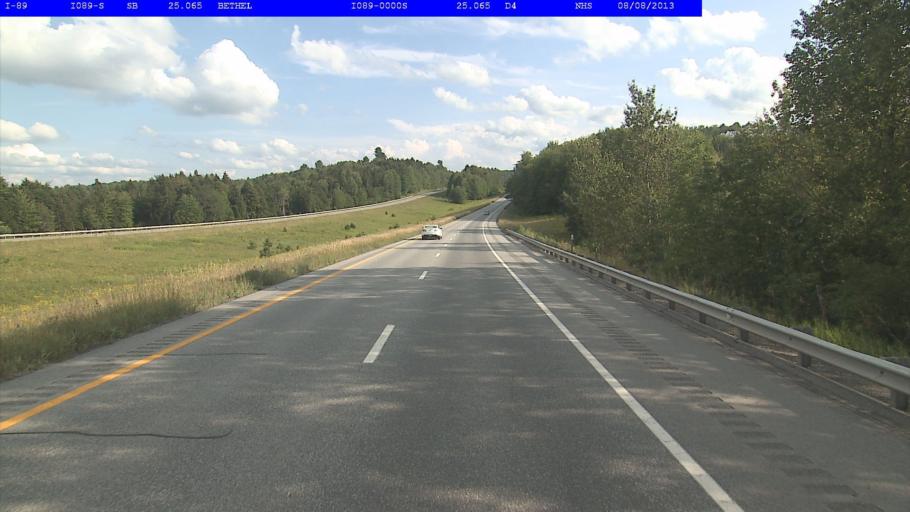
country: US
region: Vermont
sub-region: Orange County
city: Randolph
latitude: 43.8631
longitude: -72.6083
